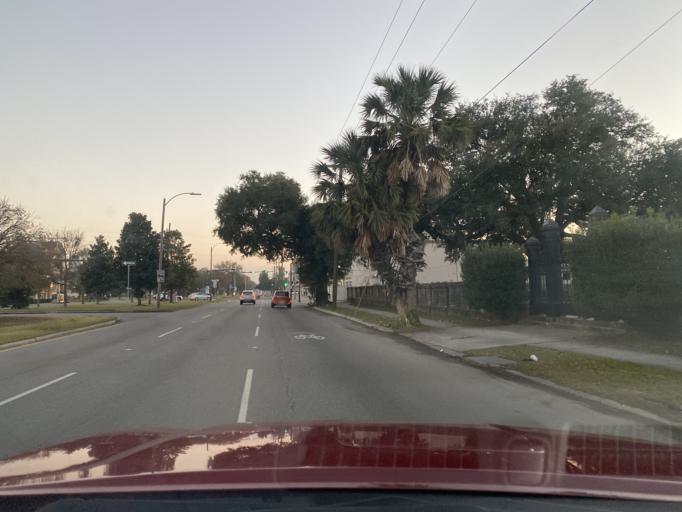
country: US
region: Louisiana
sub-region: Orleans Parish
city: New Orleans
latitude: 30.0006
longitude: -90.0595
